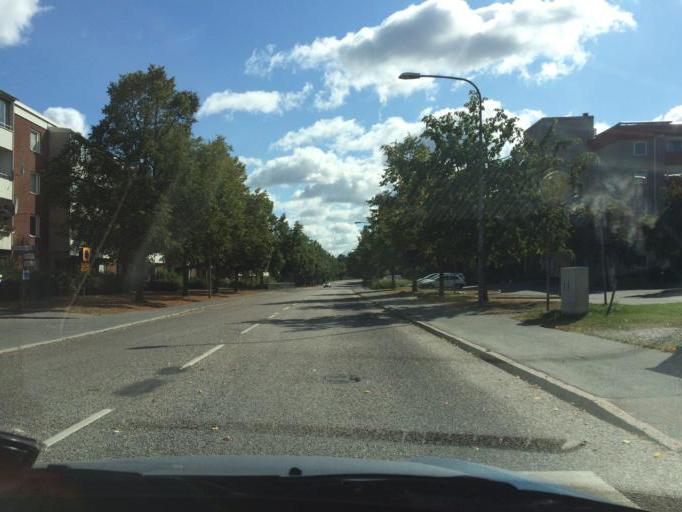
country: SE
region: Stockholm
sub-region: Nacka Kommun
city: Nacka
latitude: 59.2803
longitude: 18.1335
